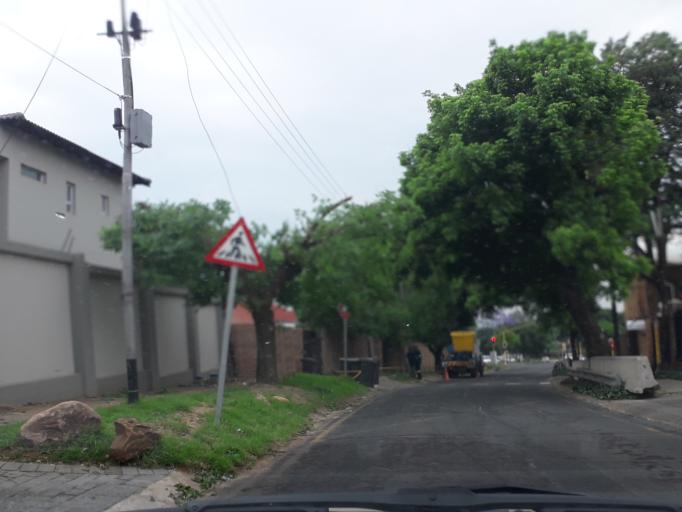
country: ZA
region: Gauteng
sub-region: City of Johannesburg Metropolitan Municipality
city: Johannesburg
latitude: -26.1391
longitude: 28.0971
